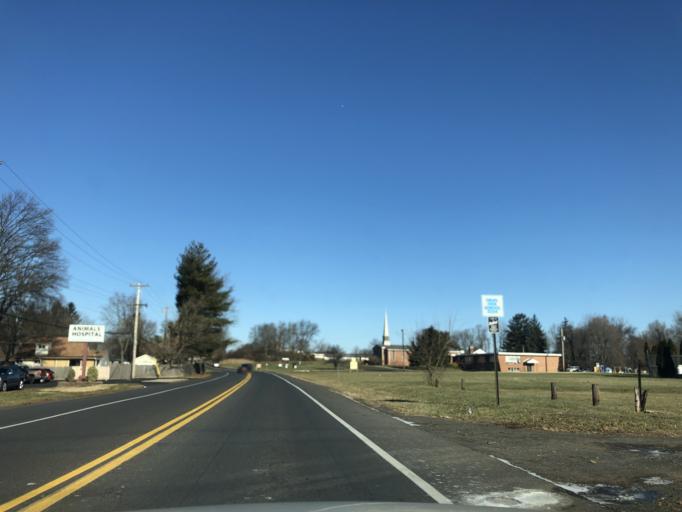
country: US
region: Pennsylvania
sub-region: Bucks County
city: Hulmeville
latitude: 40.1424
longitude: -74.8746
